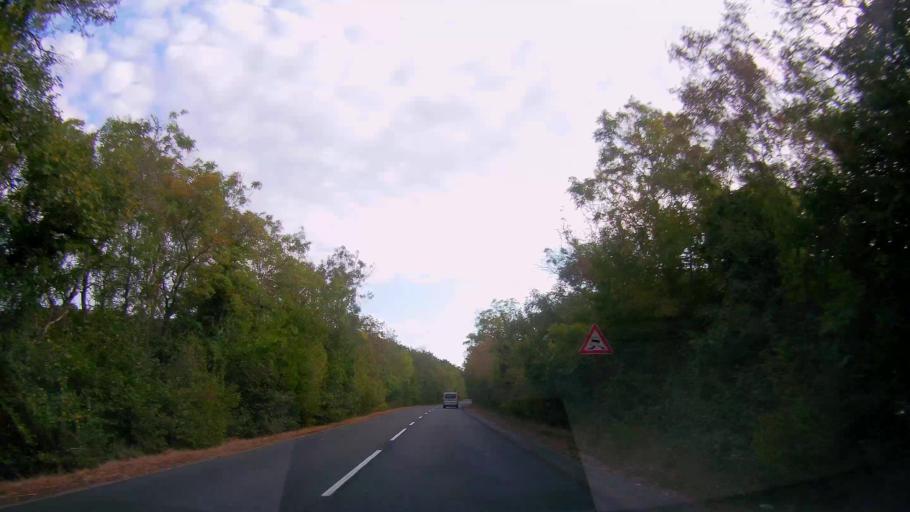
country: BG
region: Burgas
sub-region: Obshtina Primorsko
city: Primorsko
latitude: 42.3144
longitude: 27.7279
